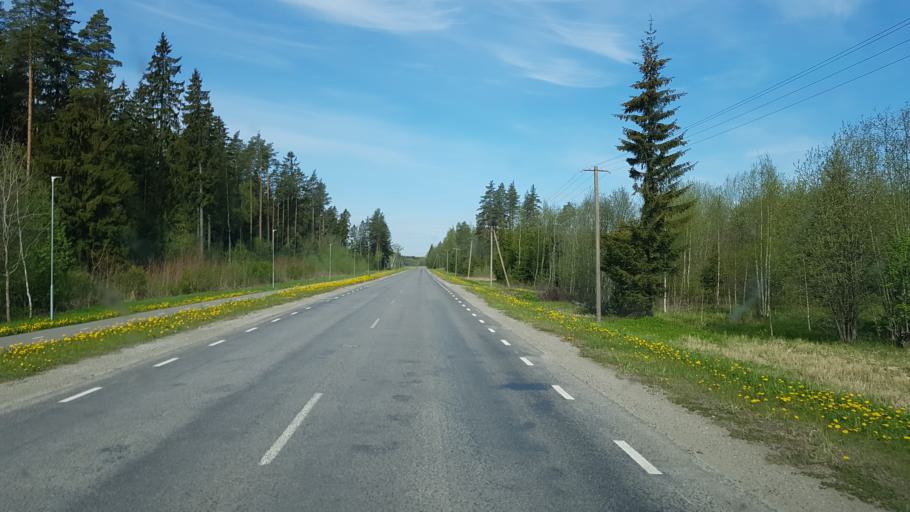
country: EE
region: Ida-Virumaa
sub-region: Kivioli linn
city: Kivioli
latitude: 59.3401
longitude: 26.9974
